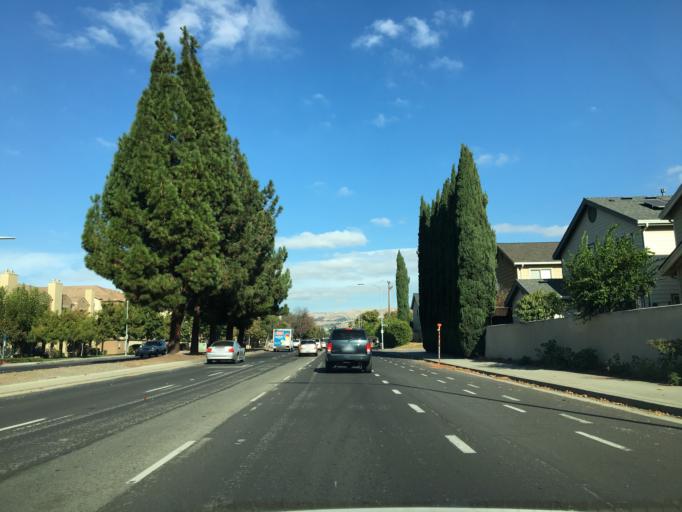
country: US
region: California
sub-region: Santa Clara County
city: Milpitas
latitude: 37.3856
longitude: -121.8888
